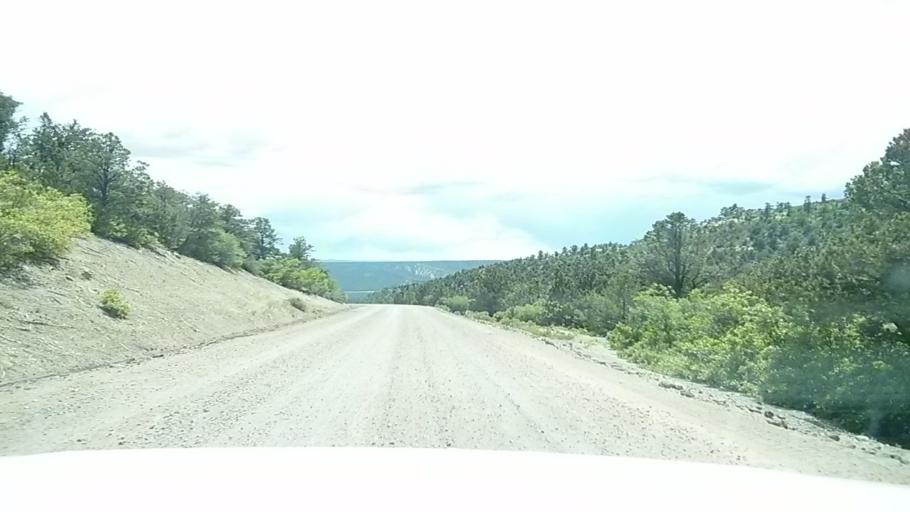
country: US
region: Utah
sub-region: Wayne County
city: Loa
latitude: 37.9202
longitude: -111.6742
